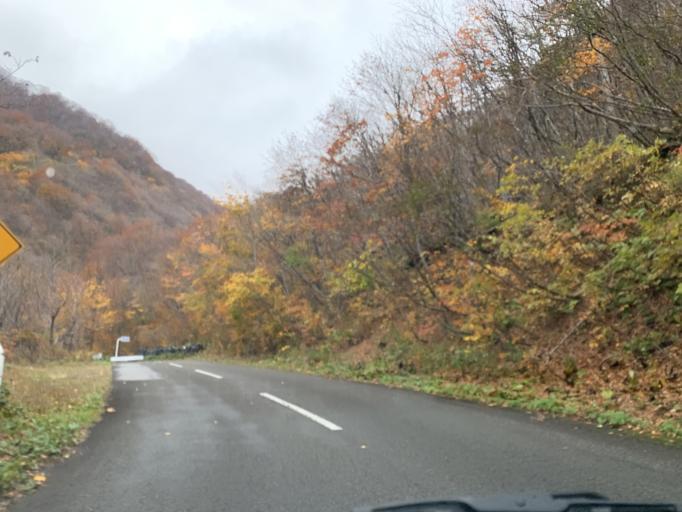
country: JP
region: Iwate
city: Mizusawa
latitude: 39.1209
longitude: 140.8334
